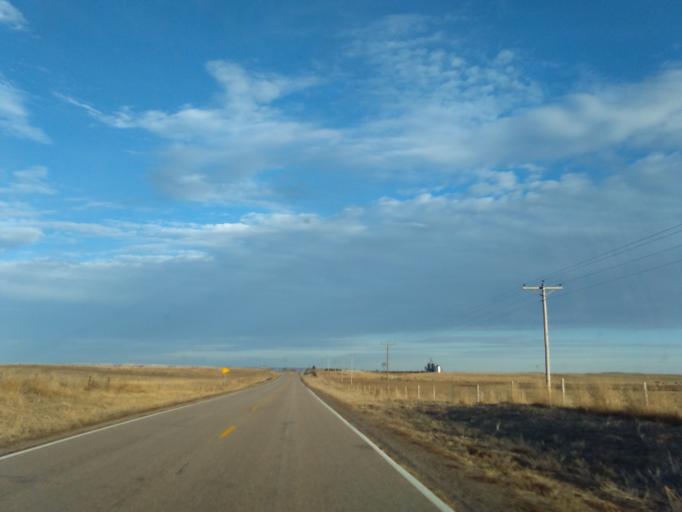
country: US
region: Nebraska
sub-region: Morrill County
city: Bridgeport
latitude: 41.5982
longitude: -102.9678
